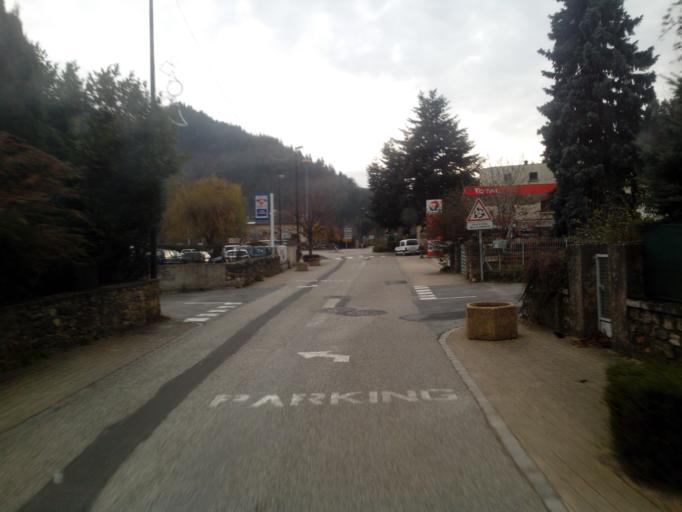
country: FR
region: Languedoc-Roussillon
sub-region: Departement de la Lozere
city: Florac
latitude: 44.3198
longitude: 3.5975
